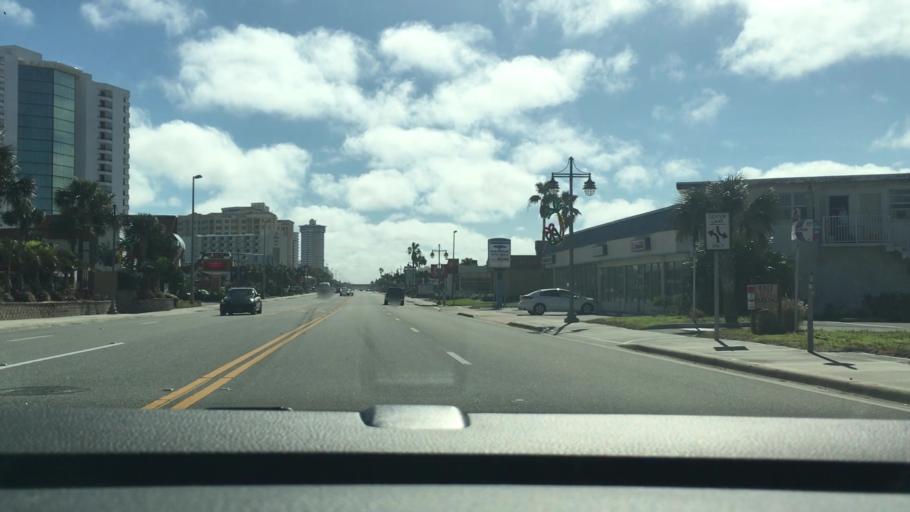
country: US
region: Florida
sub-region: Volusia County
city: Daytona Beach Shores
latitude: 29.1907
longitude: -80.9903
